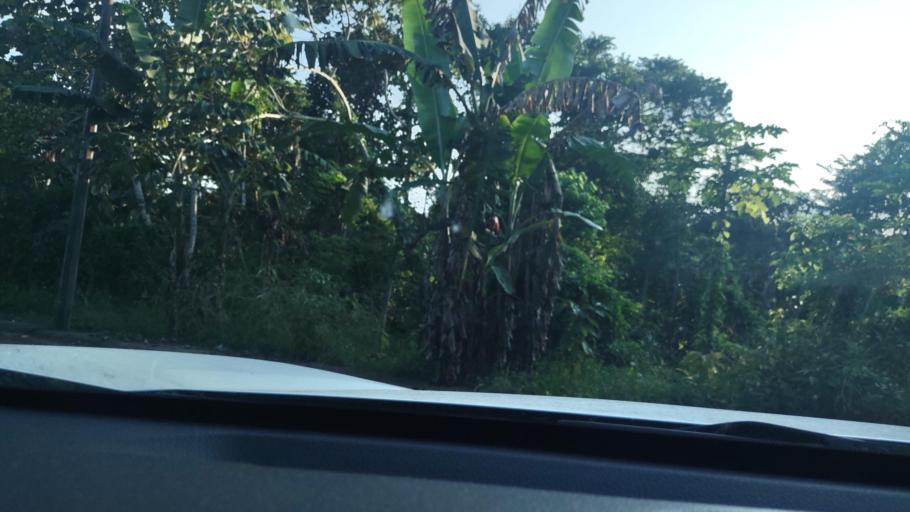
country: MX
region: Veracruz
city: Las Choapas
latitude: 17.9343
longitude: -94.1178
